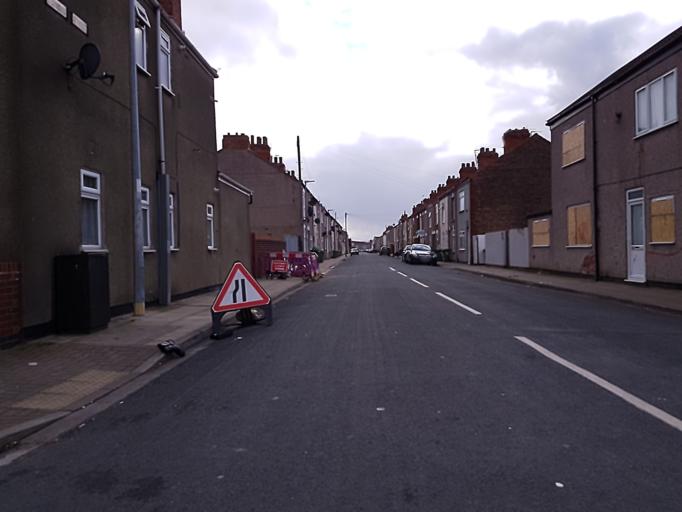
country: GB
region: England
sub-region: North East Lincolnshire
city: Grimsby
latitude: 53.5694
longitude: -0.0637
